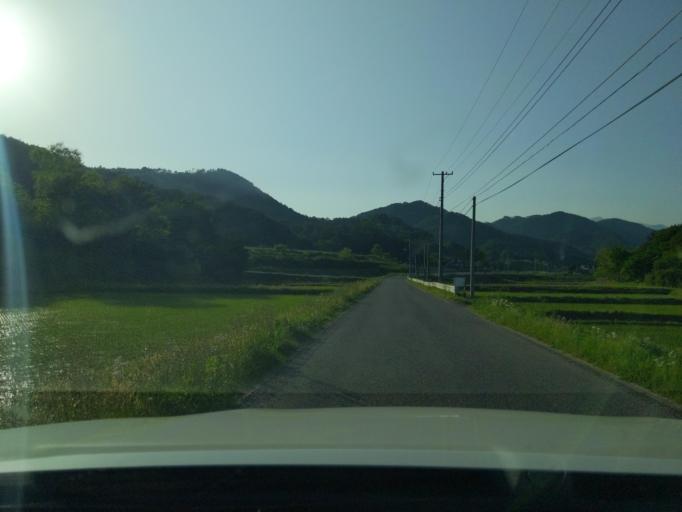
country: JP
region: Fukushima
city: Motomiya
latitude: 37.4891
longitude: 140.3301
